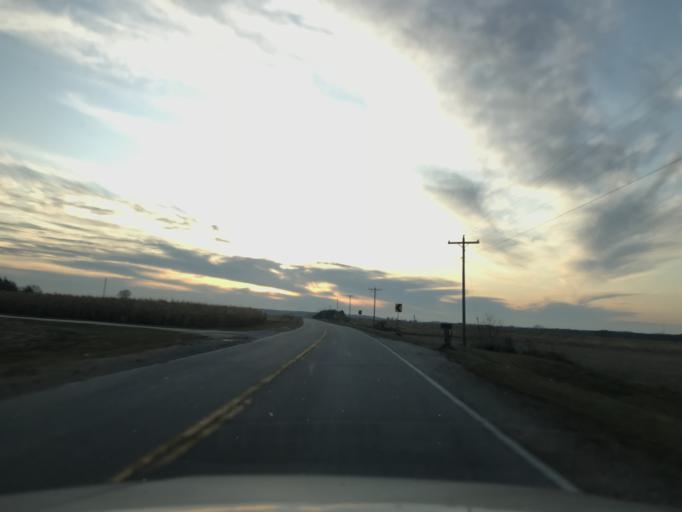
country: US
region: Illinois
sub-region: Warren County
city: Monmouth
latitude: 41.0243
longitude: -90.7793
